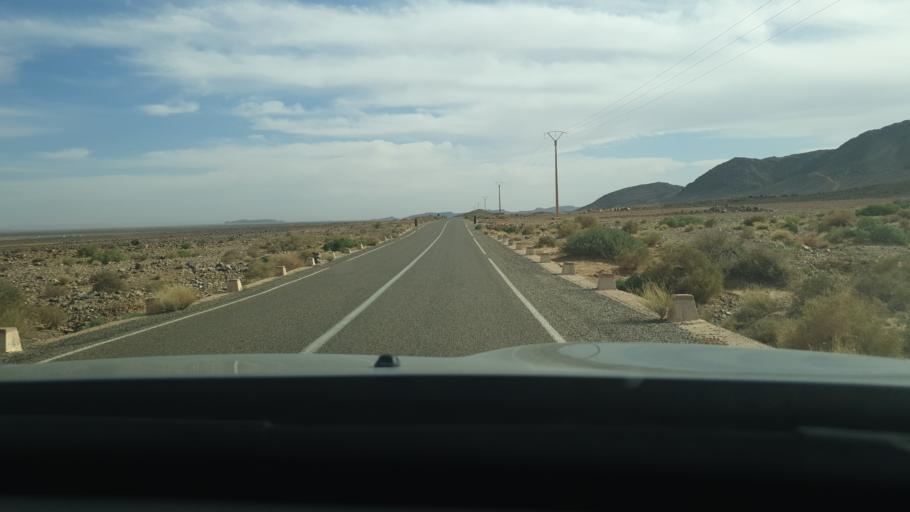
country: MA
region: Meknes-Tafilalet
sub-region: Errachidia
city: Fezna
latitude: 31.5277
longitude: -4.6334
